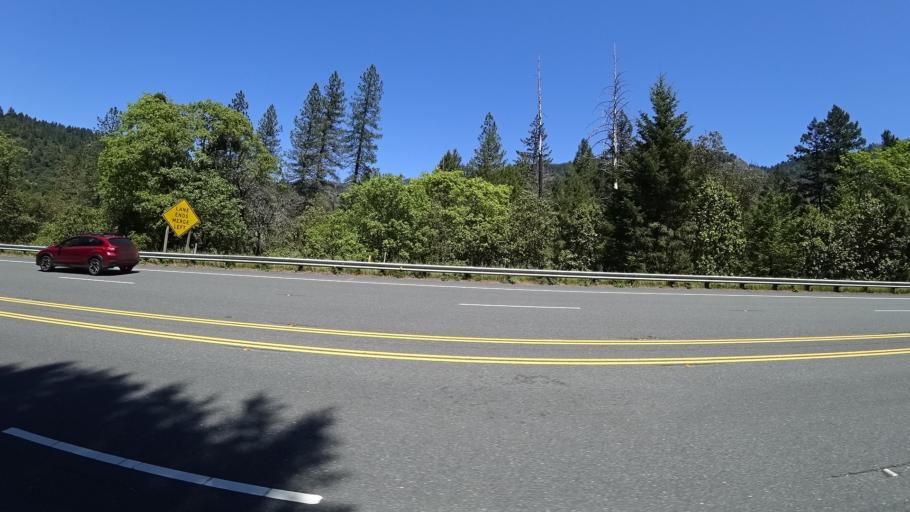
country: US
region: California
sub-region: Humboldt County
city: Willow Creek
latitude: 40.8622
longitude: -123.5010
